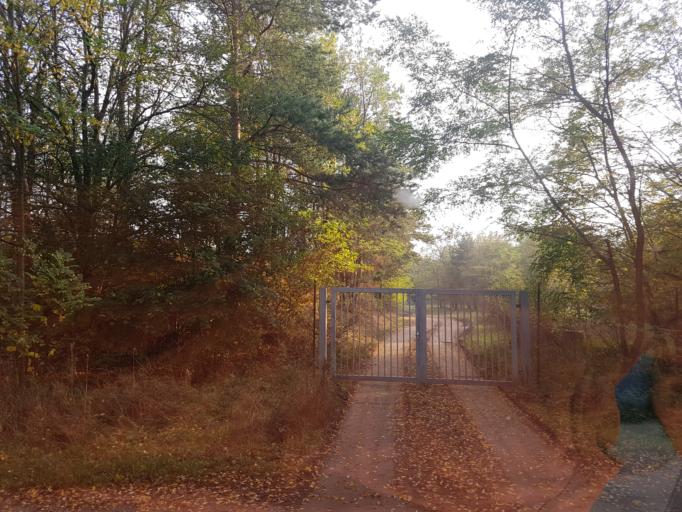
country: DE
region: Brandenburg
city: Finsterwalde
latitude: 51.6139
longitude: 13.7413
